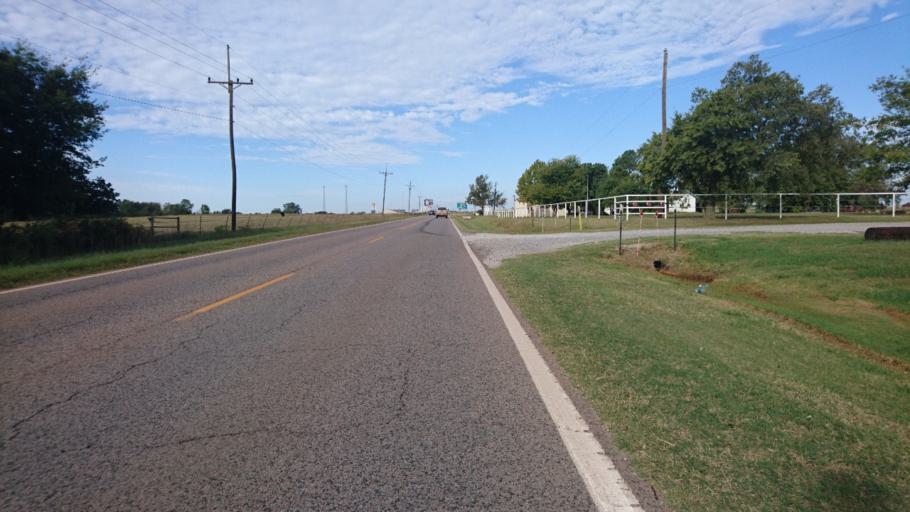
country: US
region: Oklahoma
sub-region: Lincoln County
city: Chandler
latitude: 35.6810
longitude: -97.0366
